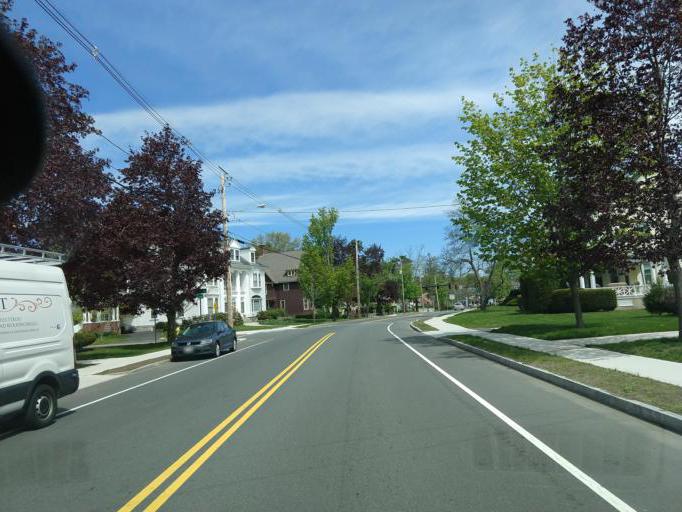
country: US
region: Massachusetts
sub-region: Essex County
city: Amesbury
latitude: 42.8497
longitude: -70.9375
